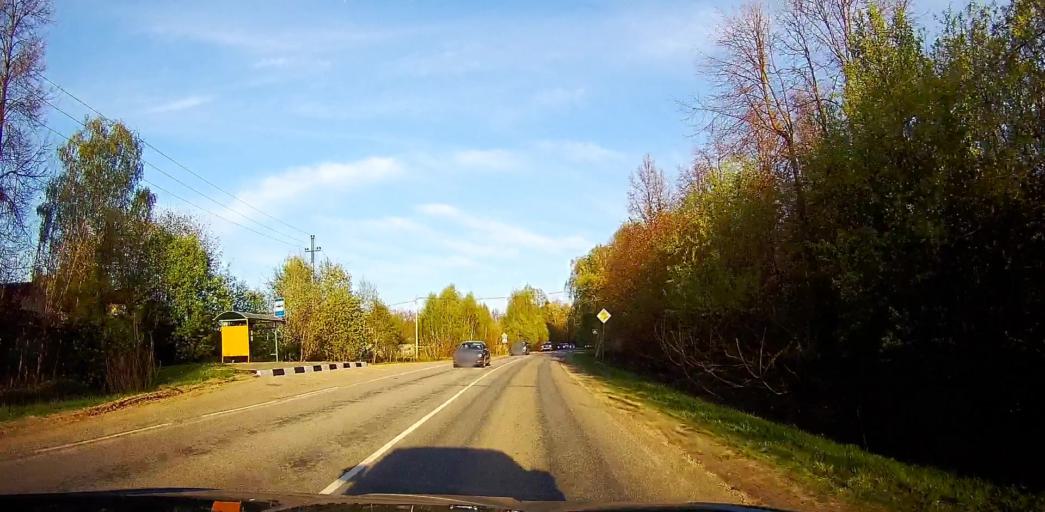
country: RU
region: Moskovskaya
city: Meshcherino
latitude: 55.2525
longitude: 38.2786
